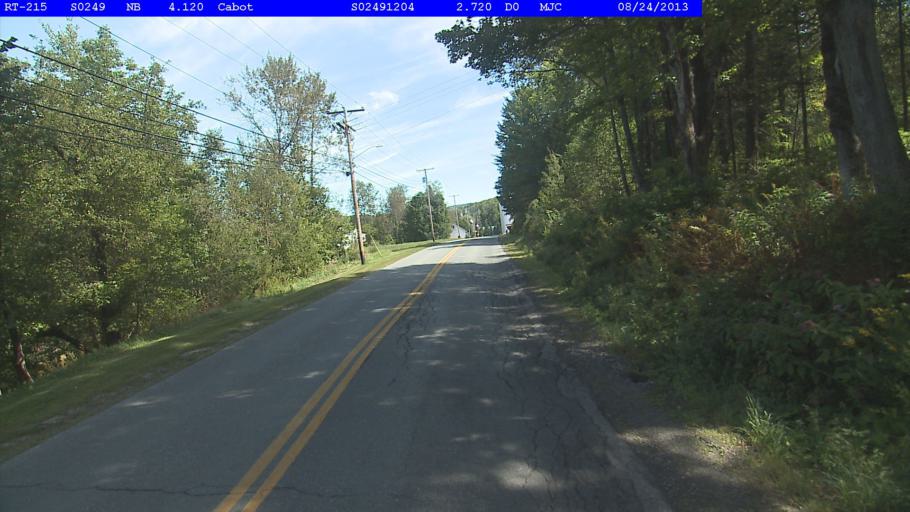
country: US
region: Vermont
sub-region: Caledonia County
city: Hardwick
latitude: 44.3997
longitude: -72.3176
